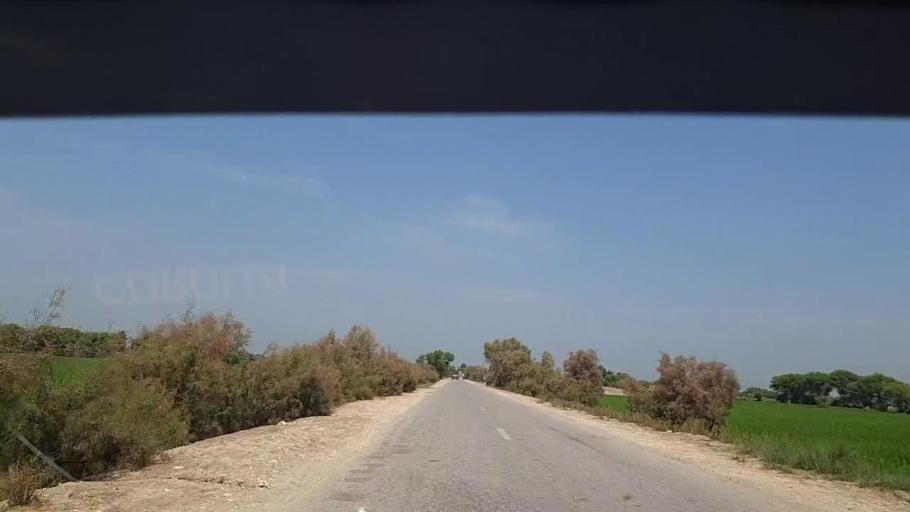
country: PK
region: Sindh
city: Thul
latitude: 28.1448
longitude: 68.8176
